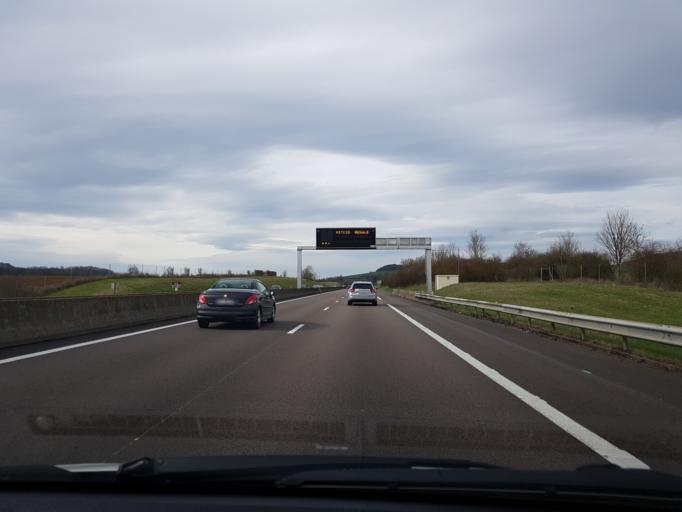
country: FR
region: Bourgogne
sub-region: Departement de la Cote-d'Or
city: Pouilly-en-Auxois
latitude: 47.2338
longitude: 4.5832
